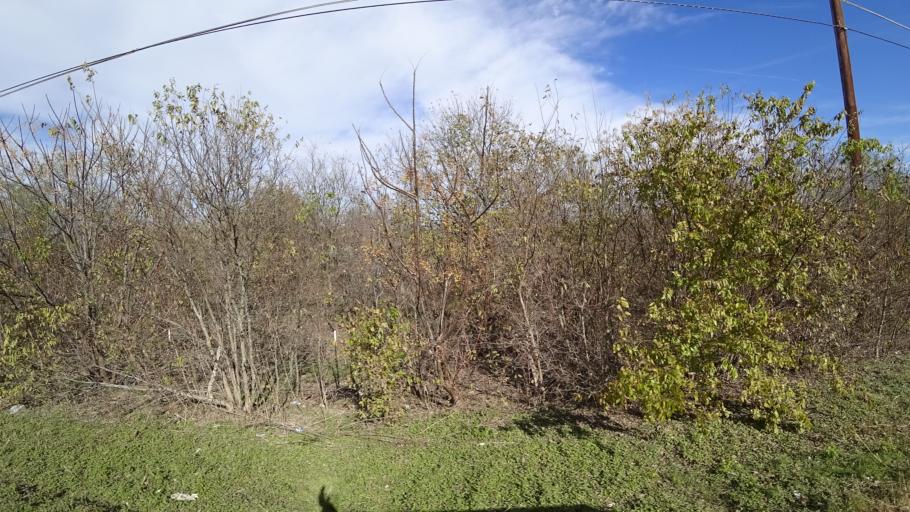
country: US
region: Texas
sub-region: Travis County
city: Onion Creek
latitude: 30.1175
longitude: -97.7077
